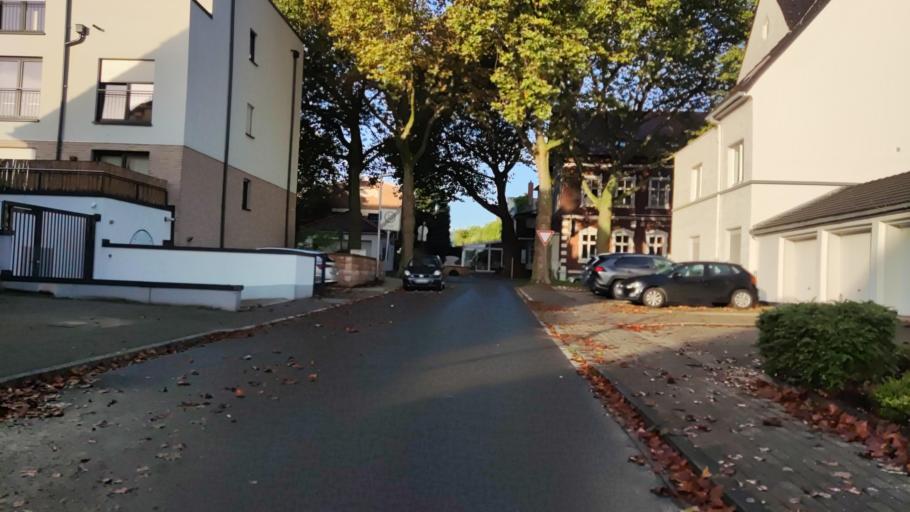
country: DE
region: North Rhine-Westphalia
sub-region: Regierungsbezirk Arnsberg
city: Herne
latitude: 51.5230
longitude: 7.2266
